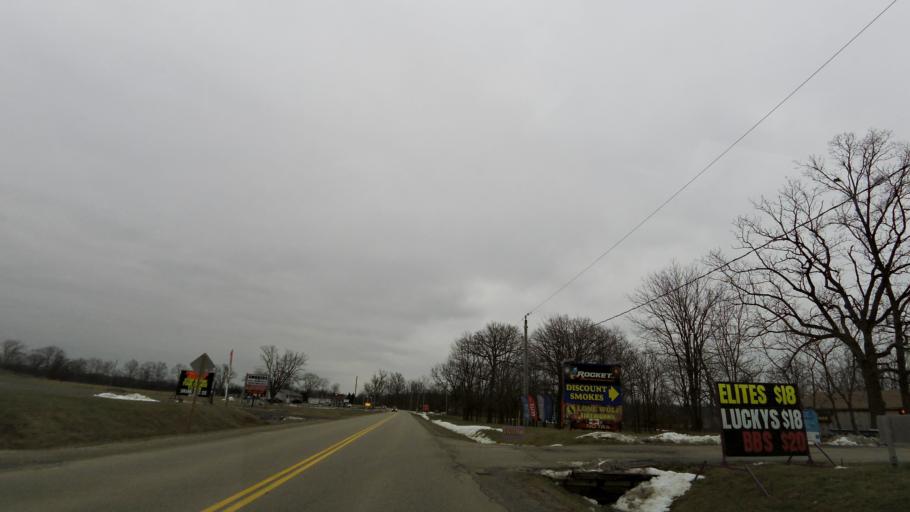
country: CA
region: Ontario
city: Ancaster
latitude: 43.1011
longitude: -80.0880
